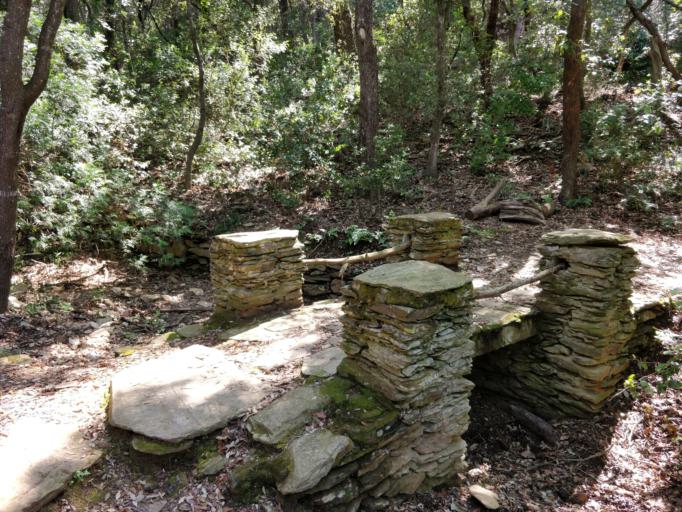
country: FR
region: Provence-Alpes-Cote d'Azur
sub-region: Departement du Var
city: Le Lavandou
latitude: 43.0043
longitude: 6.3875
